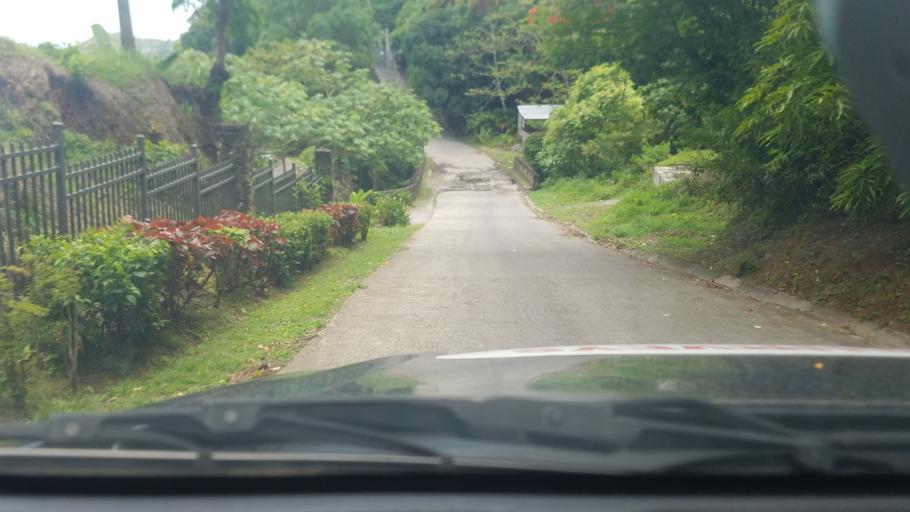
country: LC
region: Soufriere
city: Soufriere
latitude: 13.8408
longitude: -61.0619
